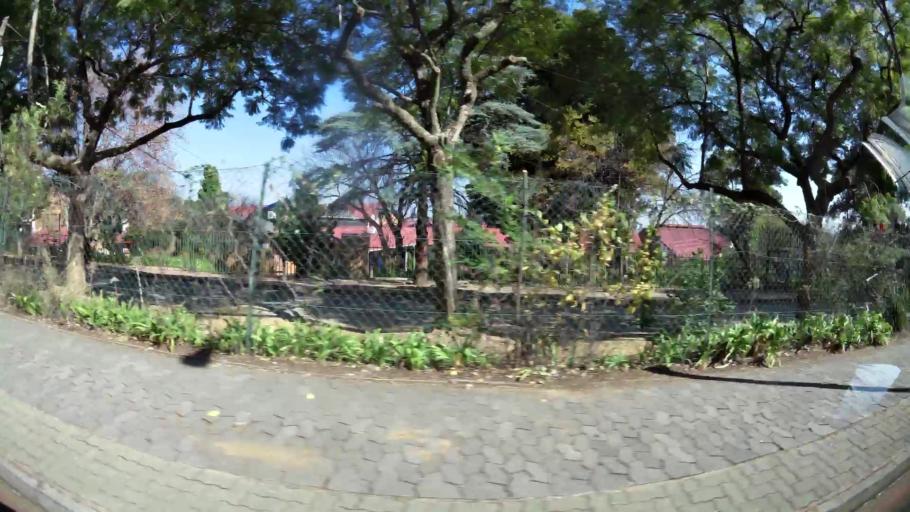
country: ZA
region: Gauteng
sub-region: City of Johannesburg Metropolitan Municipality
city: Johannesburg
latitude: -26.1234
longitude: 28.0413
